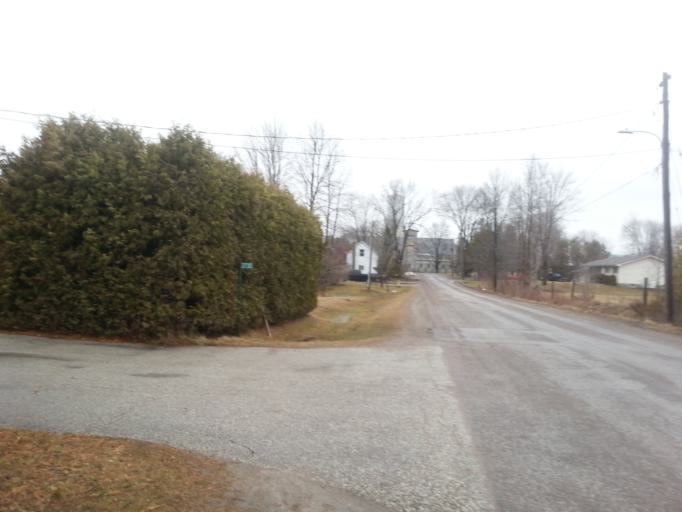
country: CA
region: Ontario
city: Orillia
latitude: 44.5457
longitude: -79.1738
